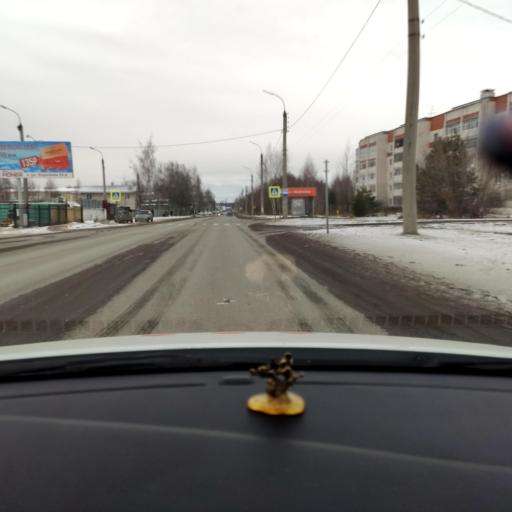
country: RU
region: Tatarstan
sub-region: Zelenodol'skiy Rayon
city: Zelenodolsk
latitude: 55.8622
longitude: 48.5504
